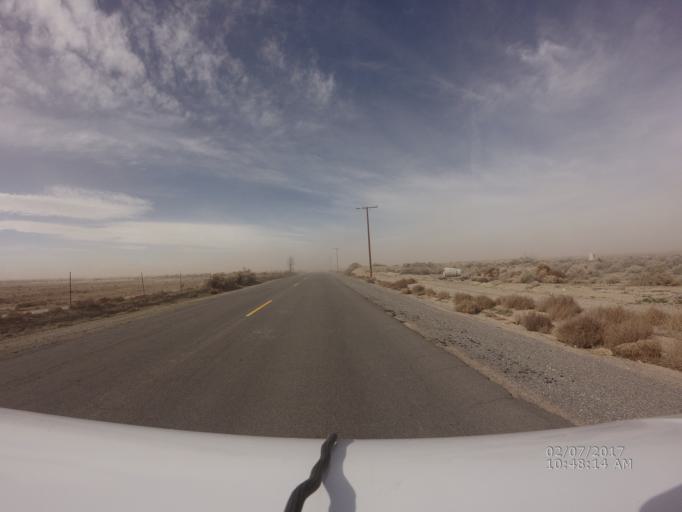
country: US
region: California
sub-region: Los Angeles County
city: Lake Los Angeles
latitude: 34.6901
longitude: -117.8663
